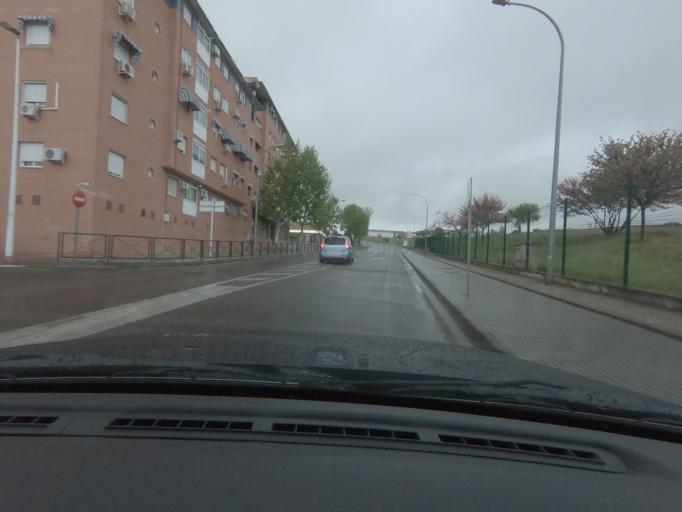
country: ES
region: Extremadura
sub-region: Provincia de Badajoz
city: Merida
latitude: 38.9242
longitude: -6.3386
